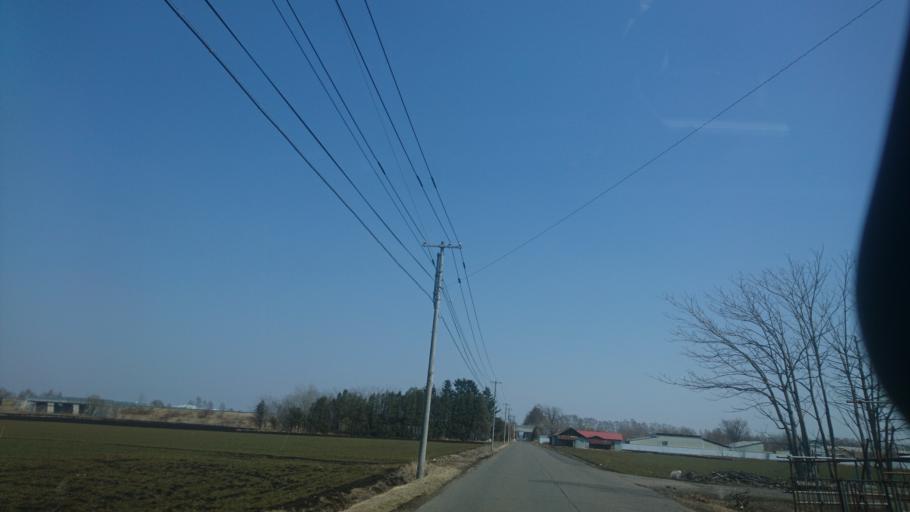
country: JP
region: Hokkaido
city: Obihiro
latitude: 42.9199
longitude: 143.1051
